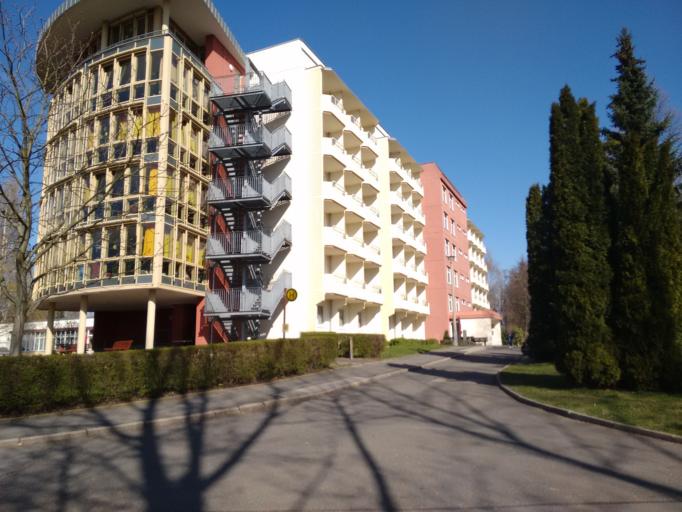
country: DE
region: Saxony
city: Limbach-Oberfrohna
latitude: 50.8527
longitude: 12.7692
